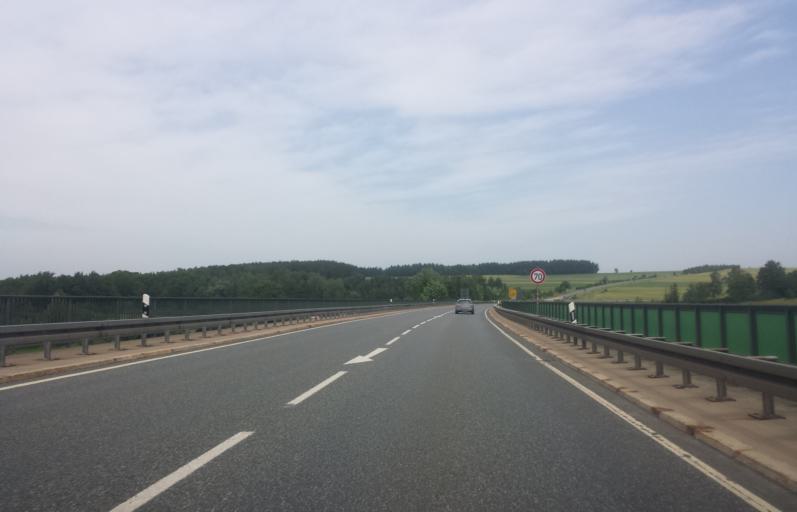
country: DE
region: Bavaria
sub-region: Upper Palatinate
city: Pressath
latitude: 49.7780
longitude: 11.9183
